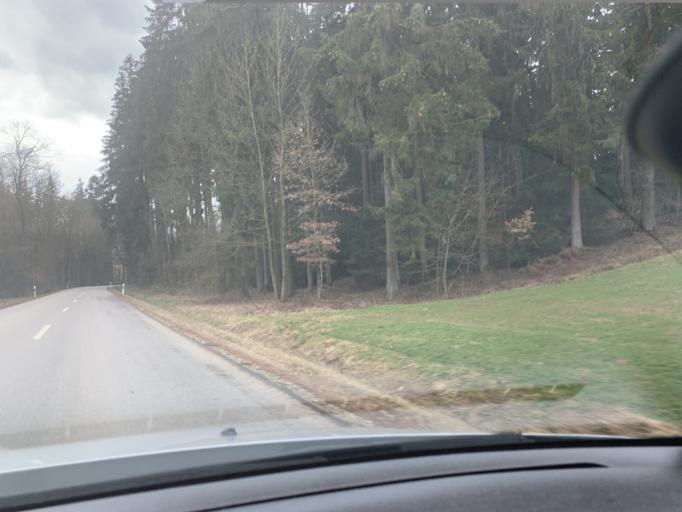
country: DE
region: Bavaria
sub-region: Lower Bavaria
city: Kumhausen
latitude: 48.5058
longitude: 12.2051
